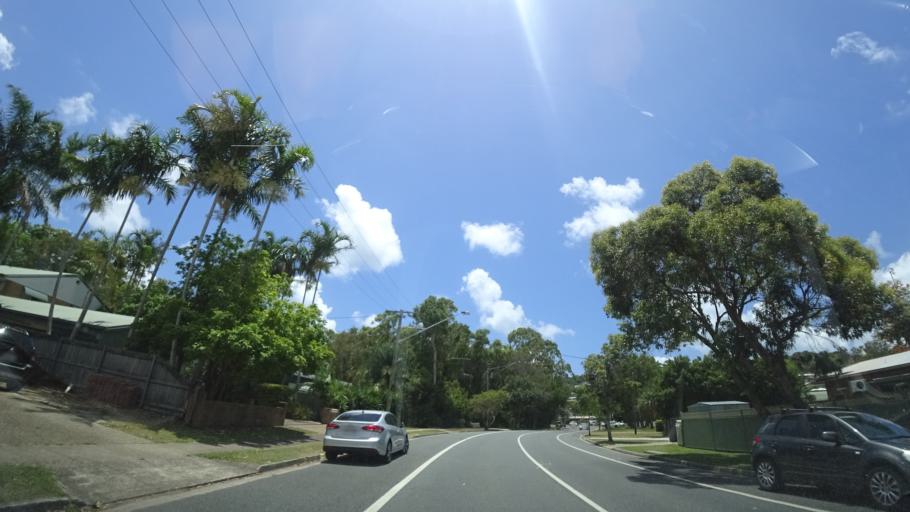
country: AU
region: Queensland
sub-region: Sunshine Coast
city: Coolum Beach
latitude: -26.5347
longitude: 153.0840
